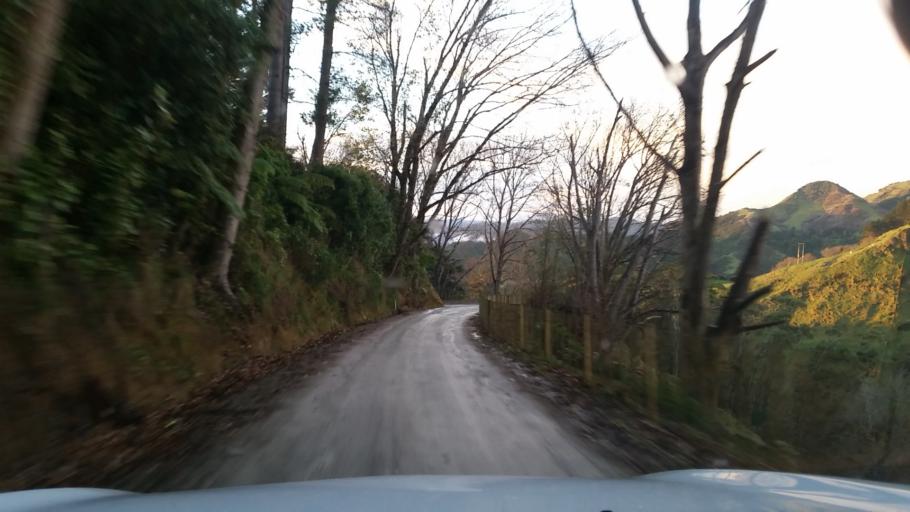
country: NZ
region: Manawatu-Wanganui
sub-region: Wanganui District
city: Wanganui
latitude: -39.7698
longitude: 174.8720
